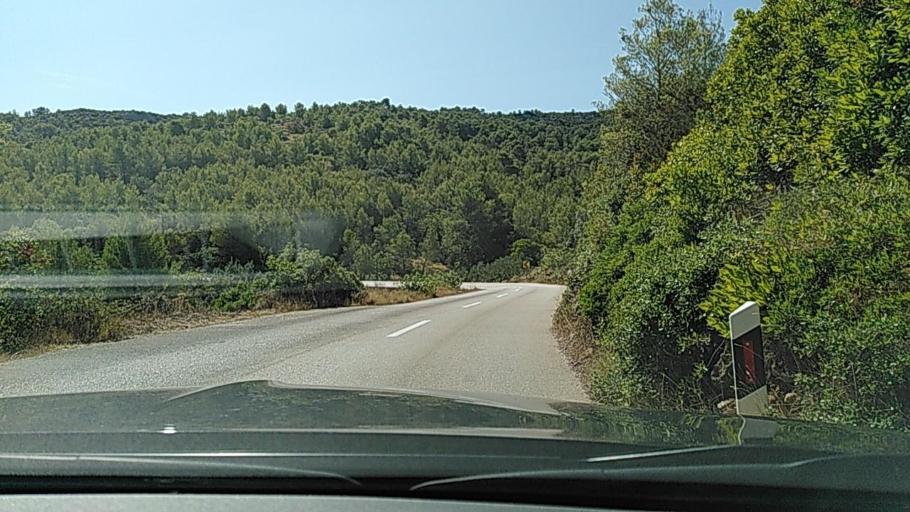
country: HR
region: Splitsko-Dalmatinska
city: Jelsa
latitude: 43.1434
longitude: 16.8109
